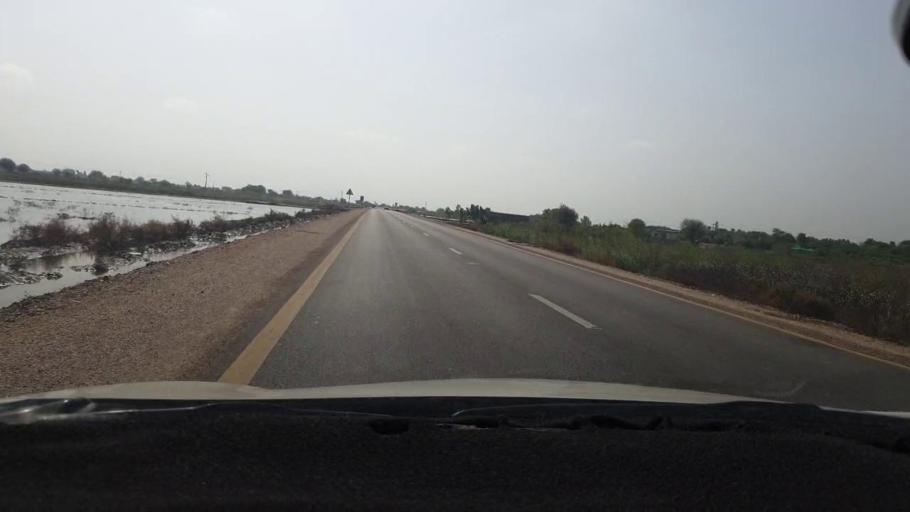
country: PK
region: Sindh
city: Jhol
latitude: 25.8616
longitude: 69.0560
